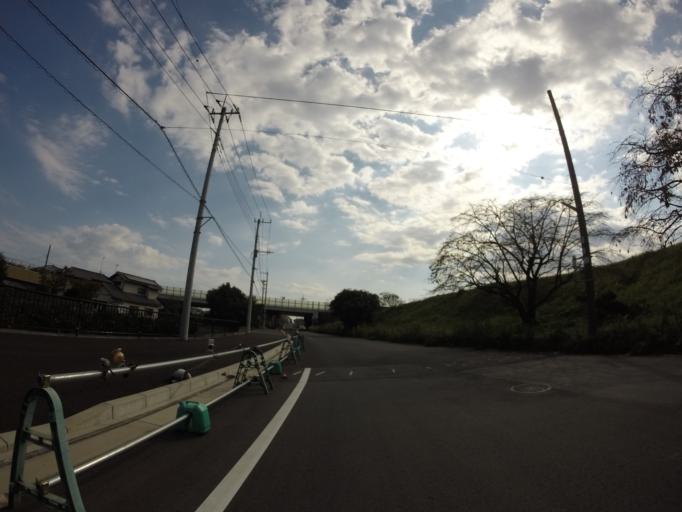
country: JP
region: Shizuoka
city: Fujinomiya
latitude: 35.1673
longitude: 138.6298
